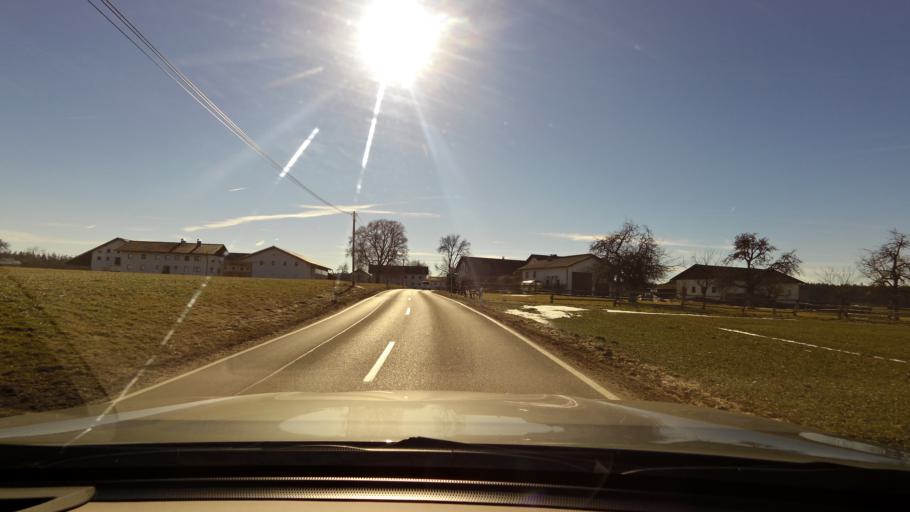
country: DE
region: Bavaria
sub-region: Upper Bavaria
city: Taufkirchen
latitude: 48.1642
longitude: 12.4587
